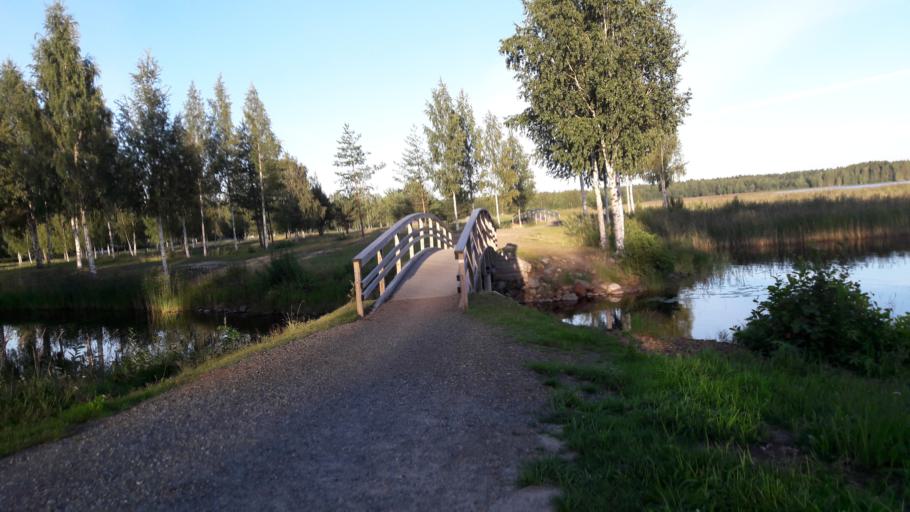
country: FI
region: North Karelia
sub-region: Joensuu
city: Joensuu
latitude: 62.6132
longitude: 29.6993
